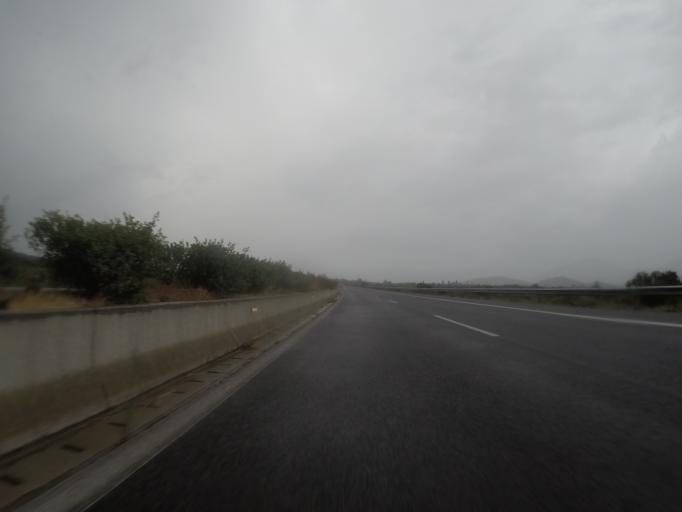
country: GR
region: Peloponnese
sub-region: Nomos Messinias
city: Meligalas
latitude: 37.2130
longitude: 22.0021
